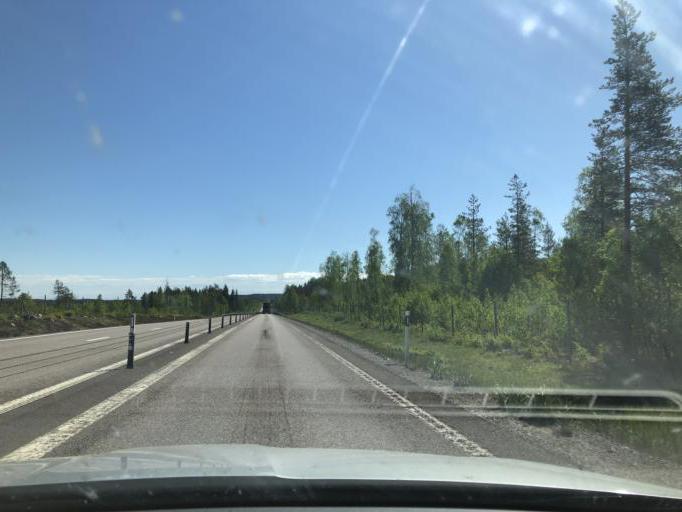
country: SE
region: Norrbotten
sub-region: Kalix Kommun
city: Toere
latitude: 65.9033
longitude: 22.8544
